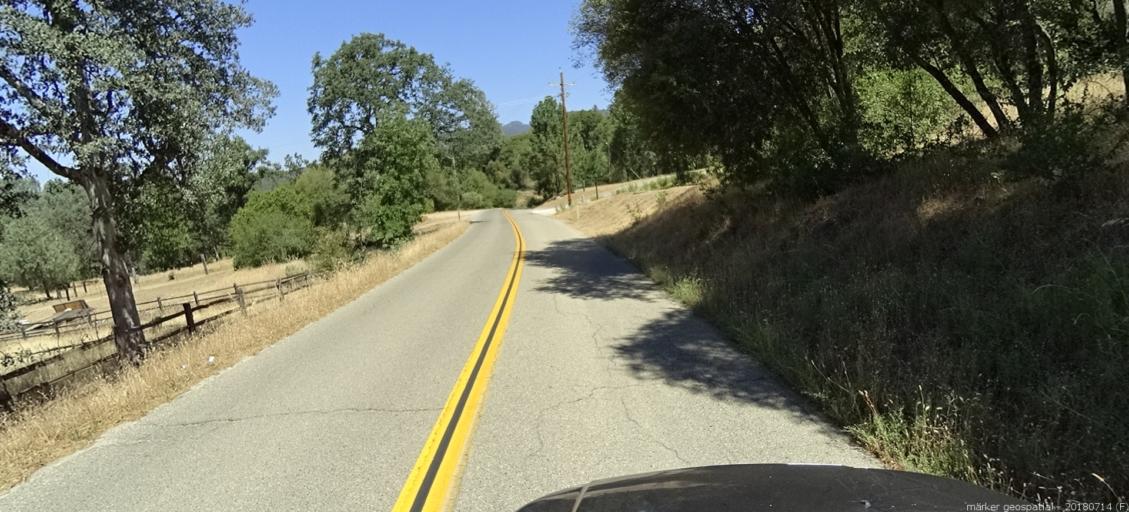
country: US
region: California
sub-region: Madera County
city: Oakhurst
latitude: 37.3724
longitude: -119.6642
